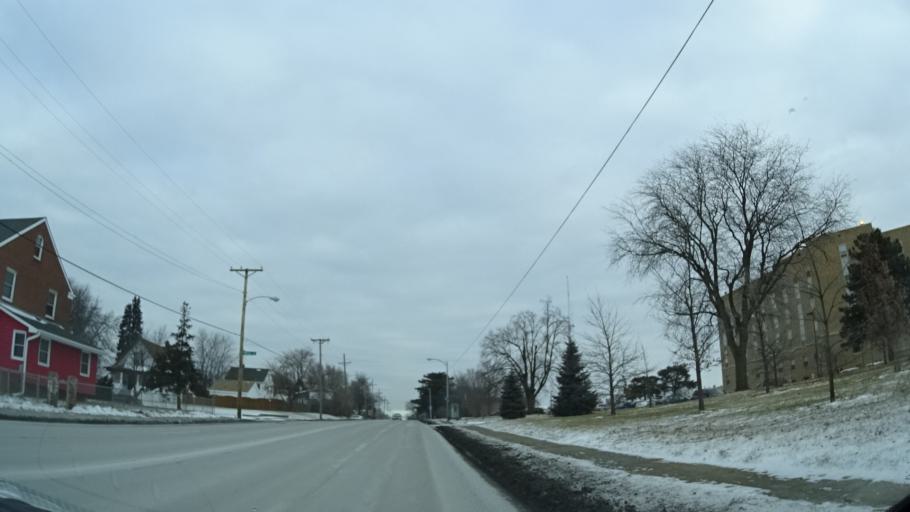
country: US
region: Nebraska
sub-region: Douglas County
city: Omaha
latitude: 41.2455
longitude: -95.9757
